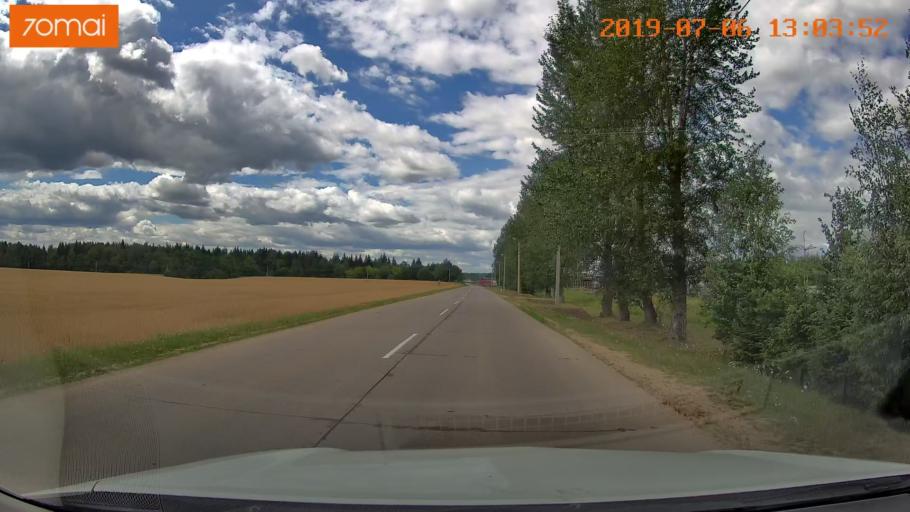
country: BY
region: Minsk
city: Dzyarzhynsk
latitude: 53.6902
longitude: 27.0944
